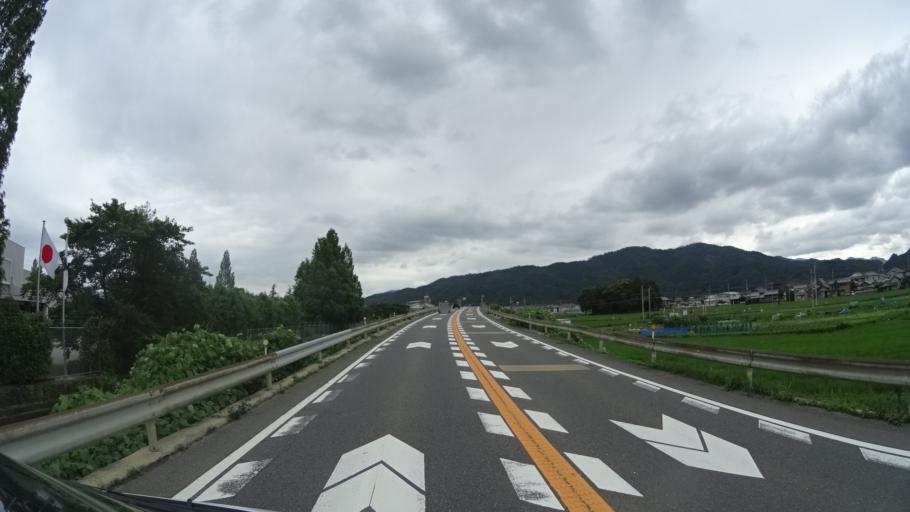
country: JP
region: Kyoto
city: Kameoka
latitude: 35.0541
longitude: 135.5483
